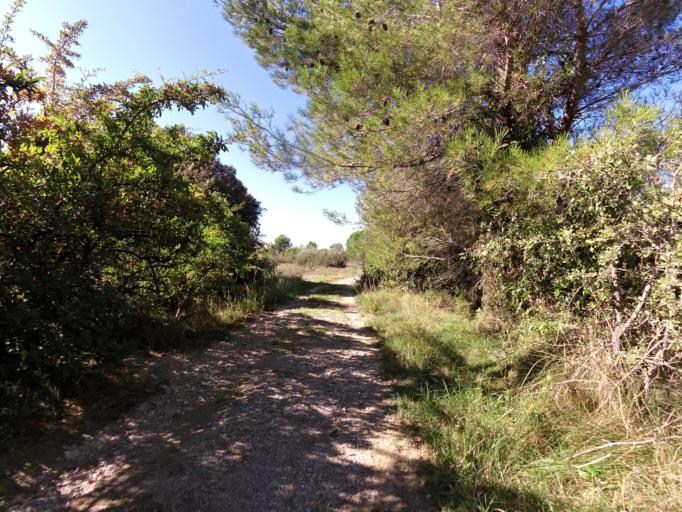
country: FR
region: Languedoc-Roussillon
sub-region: Departement de l'Herault
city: Villetelle
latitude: 43.7436
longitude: 4.1384
